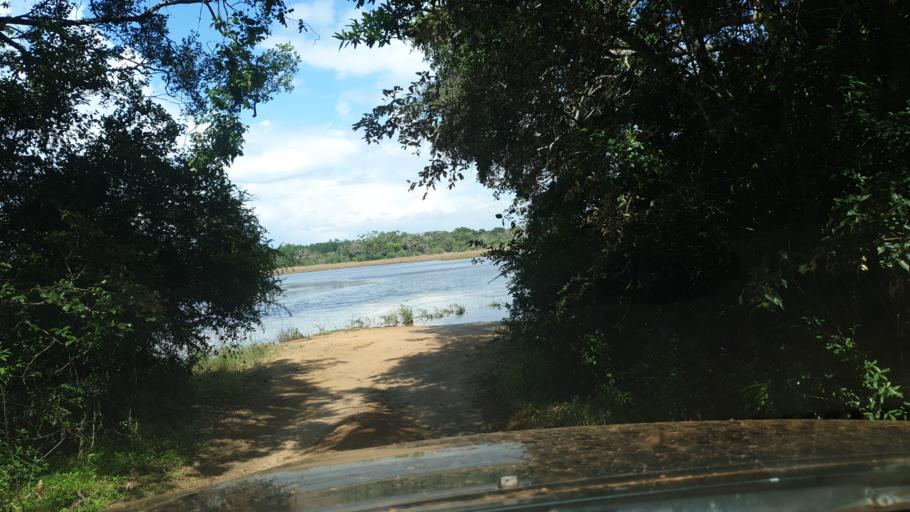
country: LK
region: North Central
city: Anuradhapura
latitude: 8.4236
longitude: 80.0114
